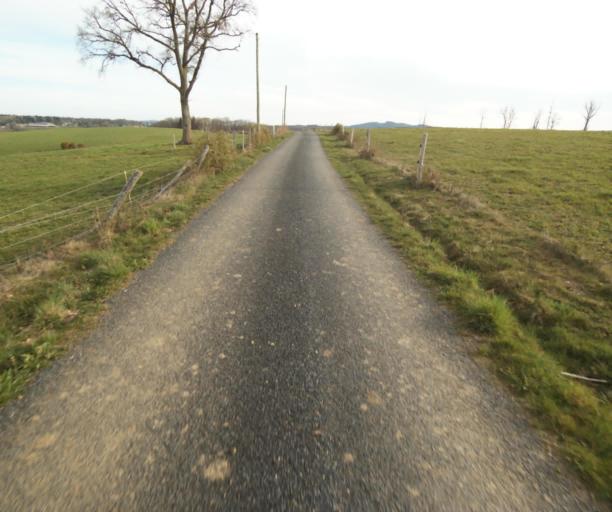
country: FR
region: Limousin
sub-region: Departement de la Correze
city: Chamboulive
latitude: 45.4559
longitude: 1.7568
